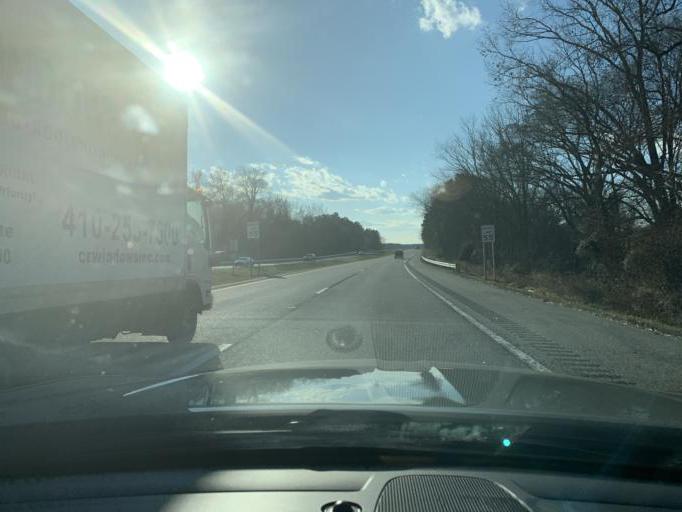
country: US
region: Maryland
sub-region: Queen Anne's County
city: Centreville
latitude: 38.9947
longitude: -76.1326
